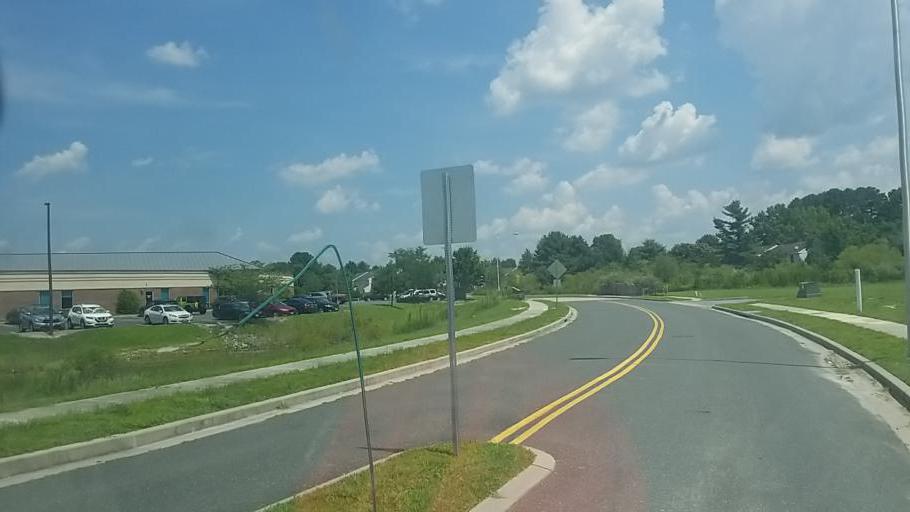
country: US
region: Maryland
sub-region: Wicomico County
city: Salisbury
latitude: 38.3624
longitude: -75.5515
